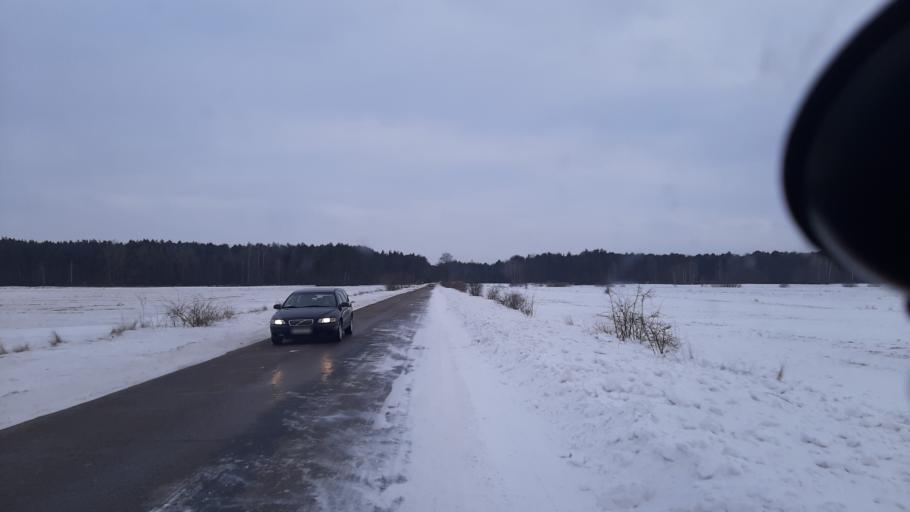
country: PL
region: Lublin Voivodeship
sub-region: Powiat lubartowski
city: Abramow
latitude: 51.4413
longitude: 22.2626
